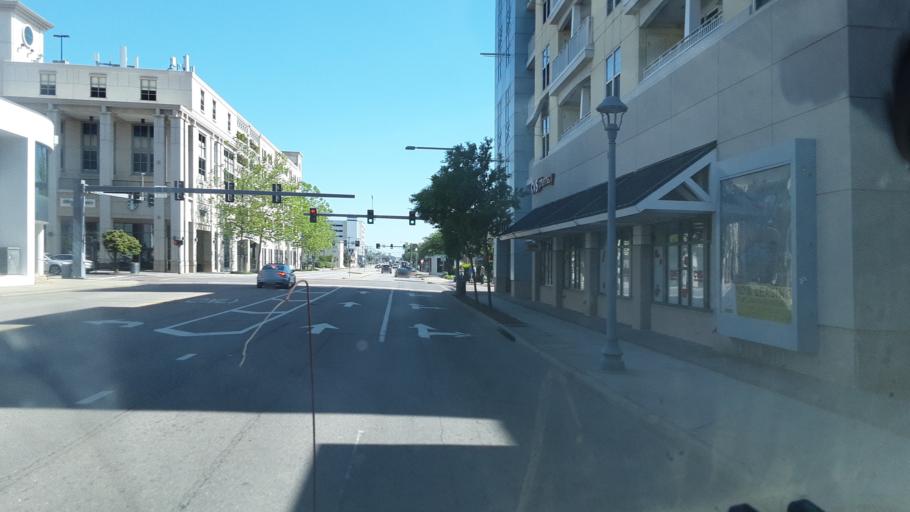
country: US
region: Virginia
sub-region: City of Virginia Beach
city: Virginia Beach
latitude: 36.8596
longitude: -75.9795
